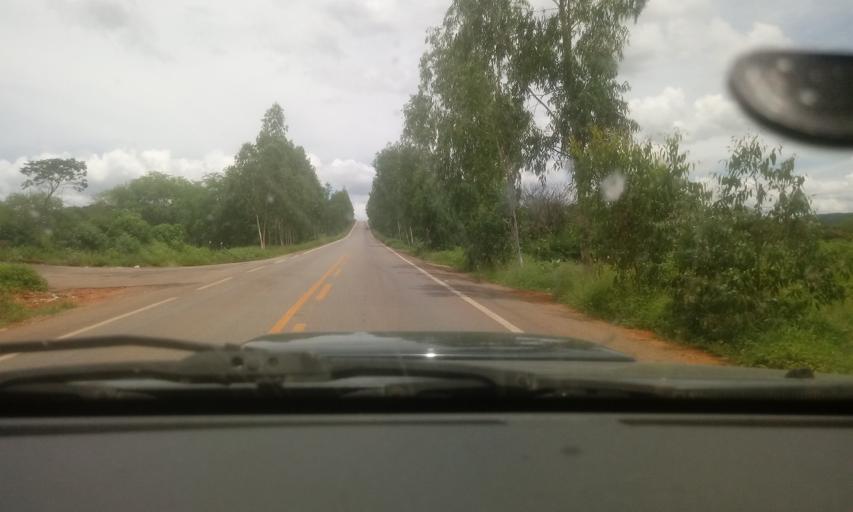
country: BR
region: Bahia
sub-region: Riacho De Santana
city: Riacho de Santana
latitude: -13.5991
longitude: -42.9437
